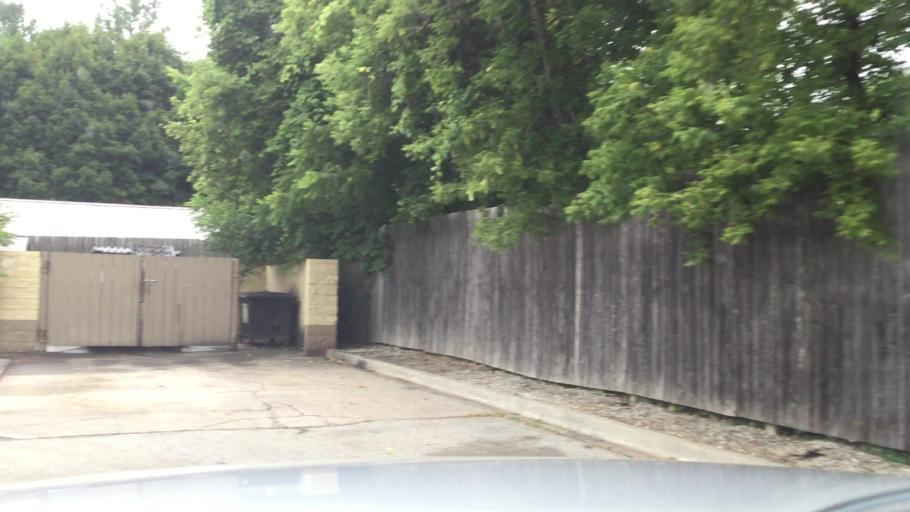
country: US
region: Michigan
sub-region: Genesee County
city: Burton
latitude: 43.0524
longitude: -83.6148
